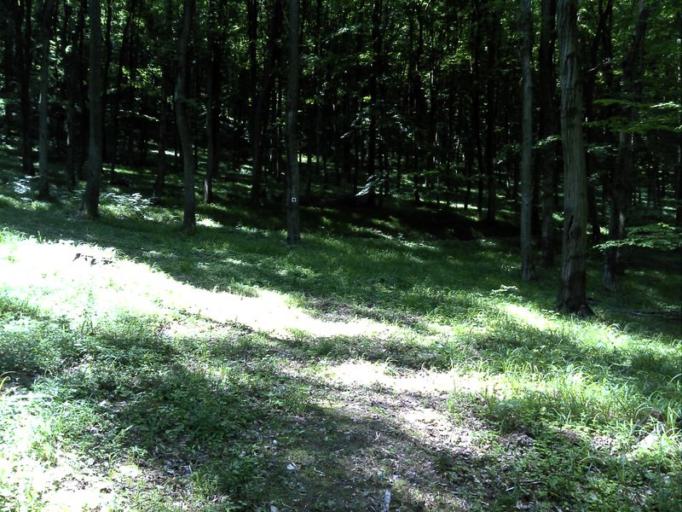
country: HU
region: Baranya
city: Buekkoesd
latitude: 46.1215
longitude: 18.0528
